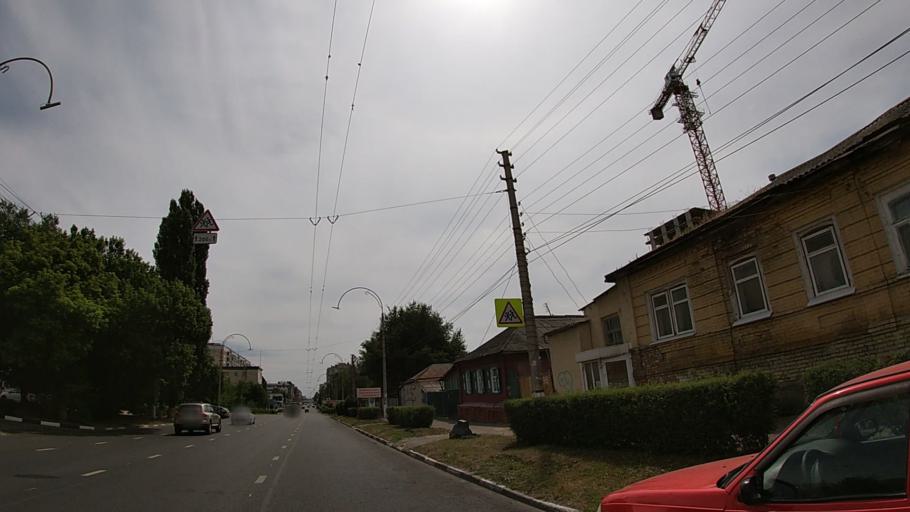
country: RU
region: Belgorod
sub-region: Belgorodskiy Rayon
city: Belgorod
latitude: 50.5994
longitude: 36.5745
